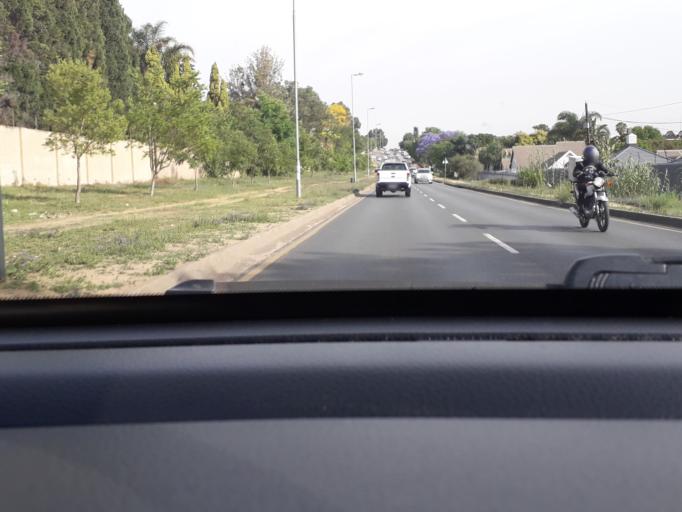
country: ZA
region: Gauteng
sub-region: City of Johannesburg Metropolitan Municipality
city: Diepsloot
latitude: -26.0351
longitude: 27.9928
